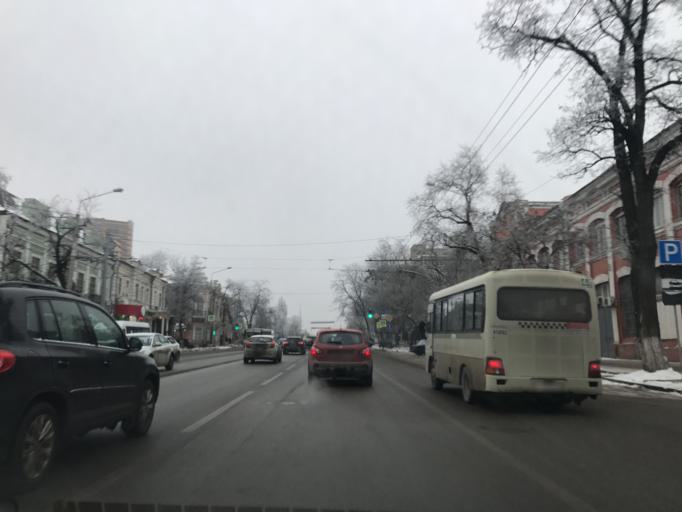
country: RU
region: Rostov
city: Rostov-na-Donu
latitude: 47.2278
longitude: 39.7042
